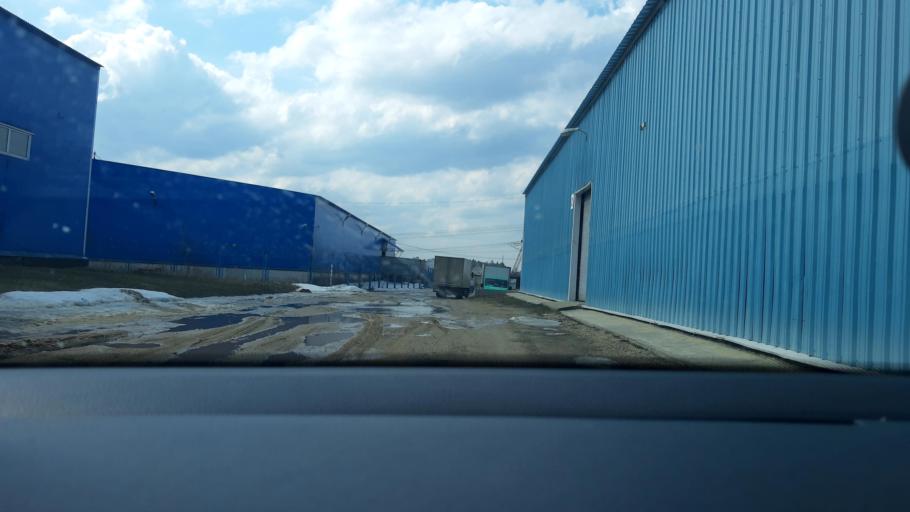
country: RU
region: Moskovskaya
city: Lesnyye Polyany
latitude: 55.9616
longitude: 37.8919
